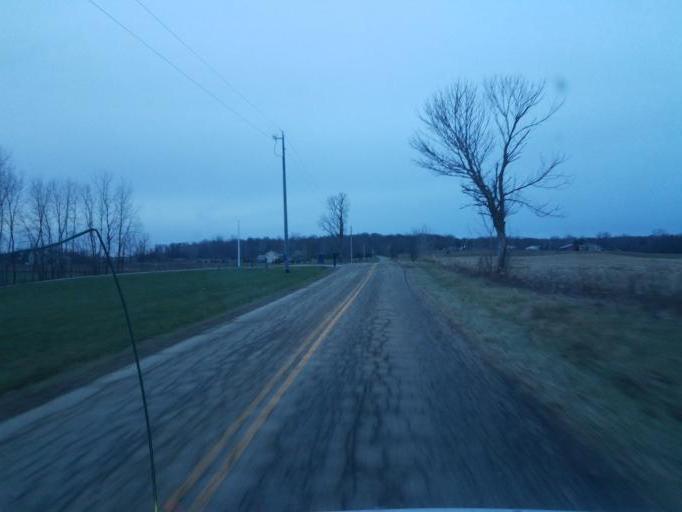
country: US
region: Ohio
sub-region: Licking County
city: Utica
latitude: 40.3047
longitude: -82.4483
